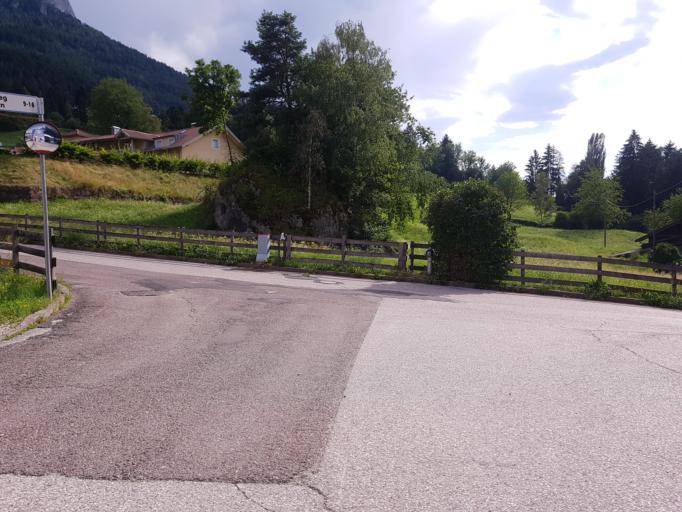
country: IT
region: Trentino-Alto Adige
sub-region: Bolzano
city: Siusi
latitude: 46.5411
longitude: 11.5569
